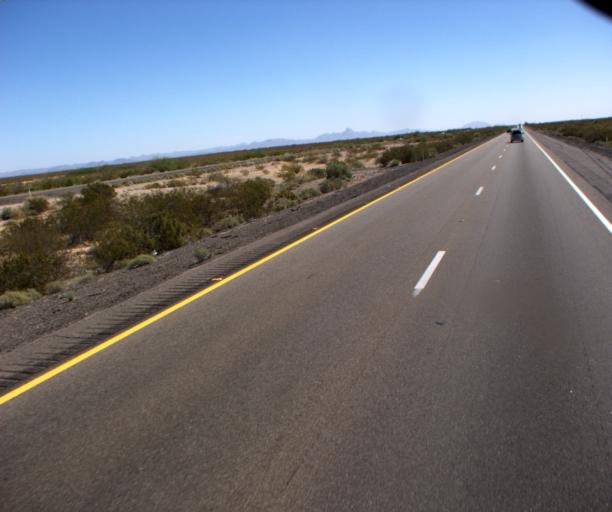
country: US
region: Arizona
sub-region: La Paz County
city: Salome
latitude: 33.5862
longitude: -113.4693
